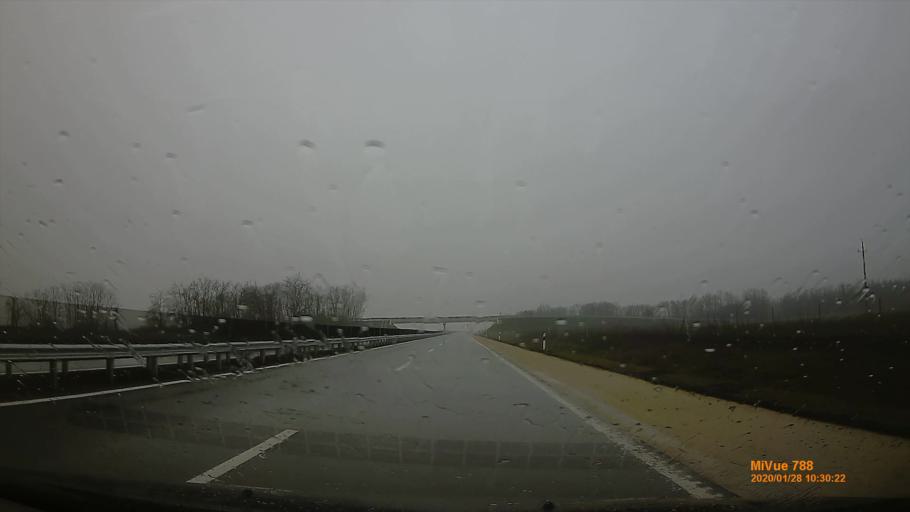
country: HU
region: Pest
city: Gomba
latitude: 47.3312
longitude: 19.5192
